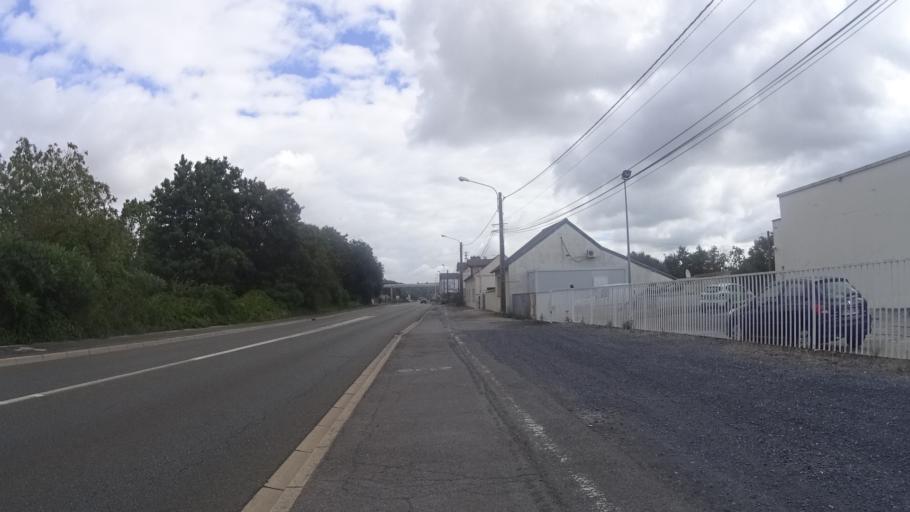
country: FR
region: Picardie
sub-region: Departement de l'Oise
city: Clairoix
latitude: 49.4309
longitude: 2.8372
